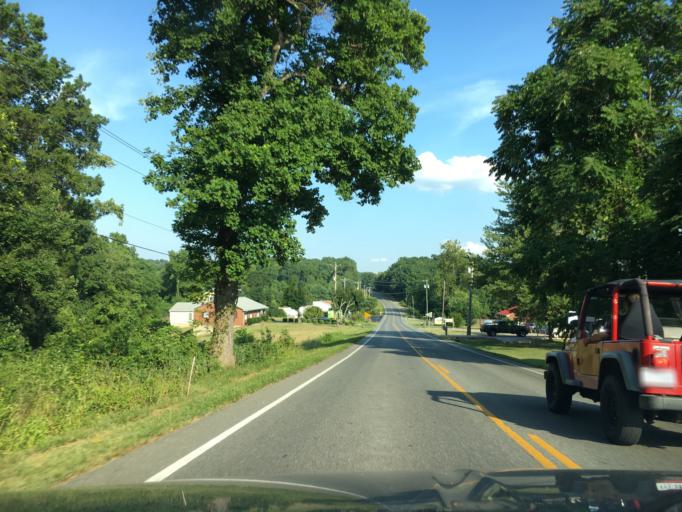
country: US
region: Virginia
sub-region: Franklin County
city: Union Hall
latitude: 37.0080
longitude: -79.7794
